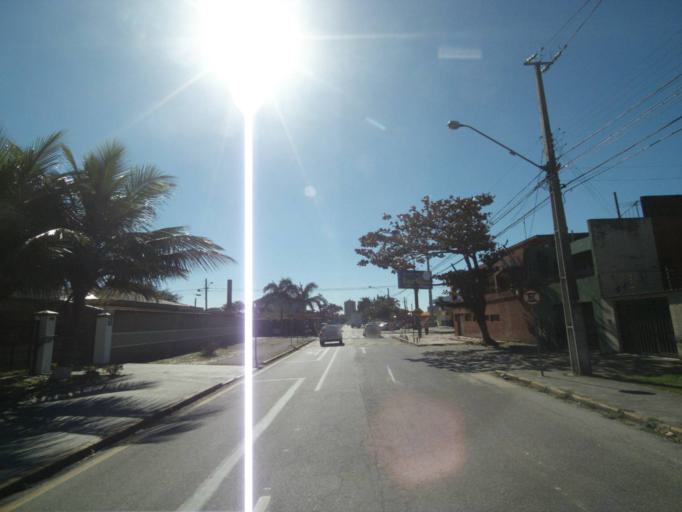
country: BR
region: Parana
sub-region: Paranagua
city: Paranagua
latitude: -25.5273
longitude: -48.5228
